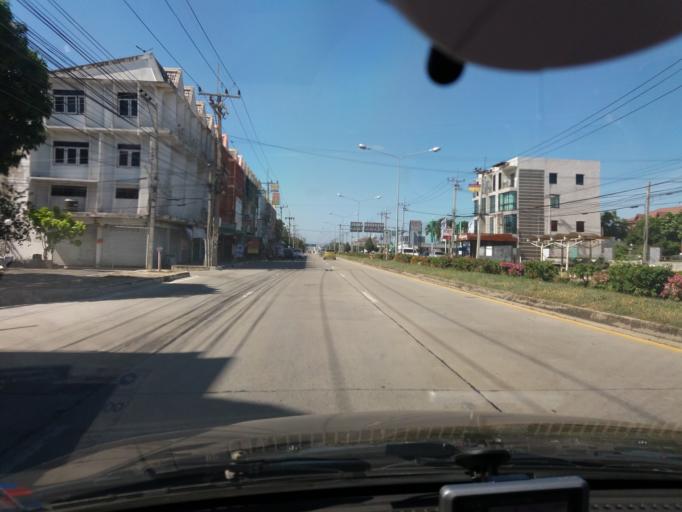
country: TH
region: Suphan Buri
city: Suphan Buri
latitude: 14.4633
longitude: 100.1409
